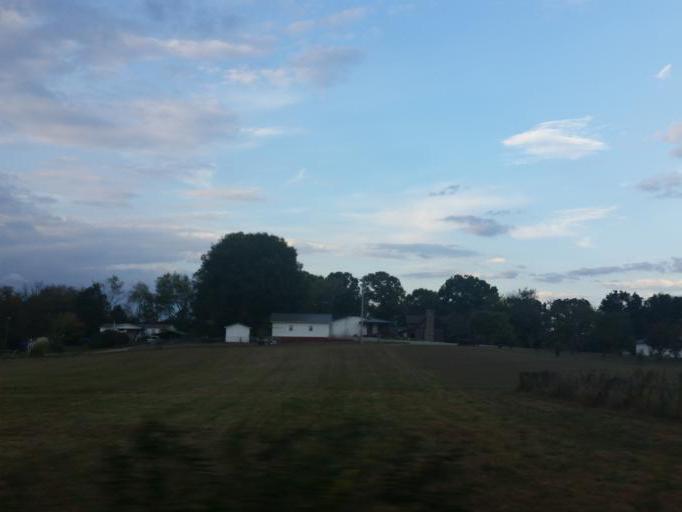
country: US
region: Tennessee
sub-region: Blount County
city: Louisville
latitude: 35.7704
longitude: -84.0295
